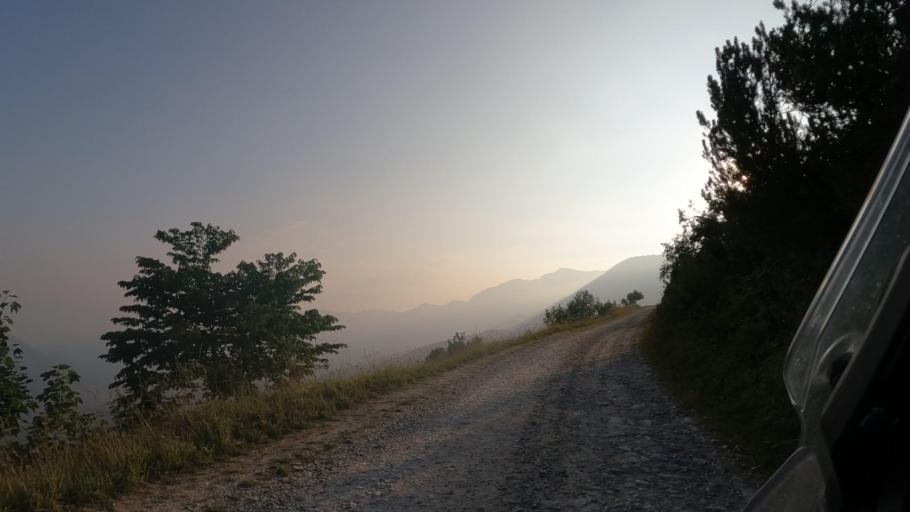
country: IT
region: Piedmont
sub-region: Provincia di Cuneo
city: Limone Piemonte
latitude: 44.1533
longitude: 7.5745
